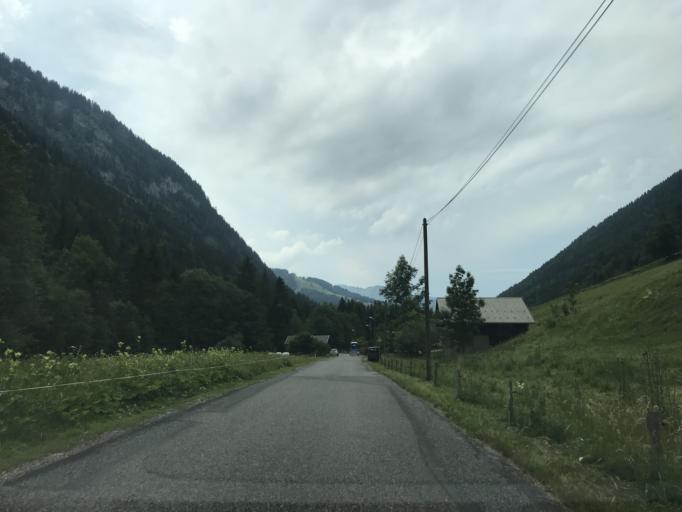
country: FR
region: Rhone-Alpes
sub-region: Departement de la Haute-Savoie
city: Morzine
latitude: 46.1537
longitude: 6.7380
